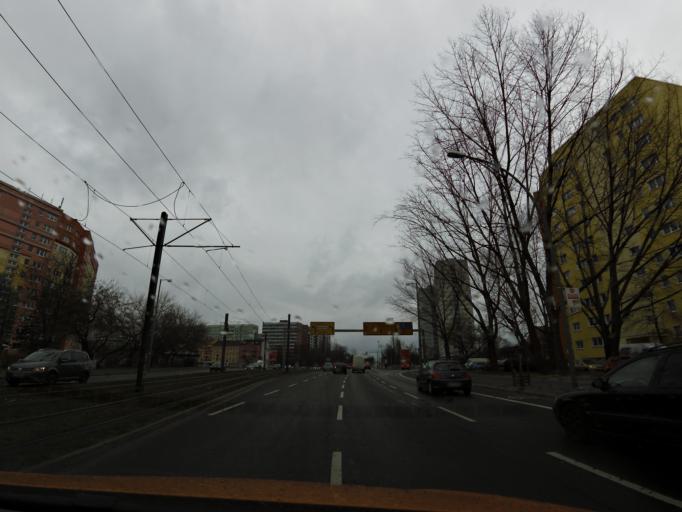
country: DE
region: Berlin
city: Friedrichsfelde
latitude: 52.5081
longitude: 13.5193
